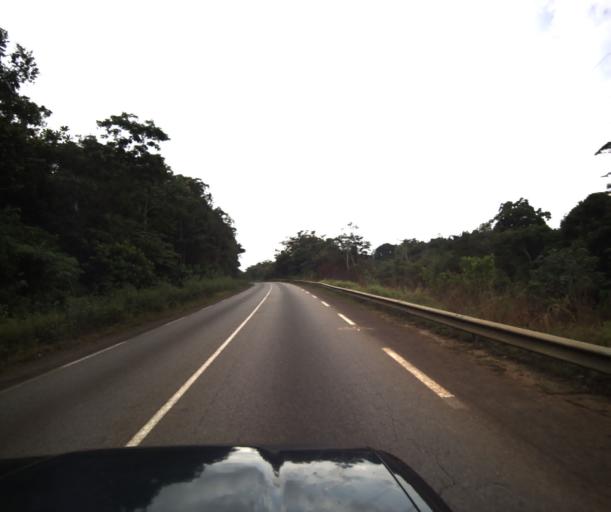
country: CM
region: Littoral
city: Edea
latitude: 3.8164
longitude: 10.3387
